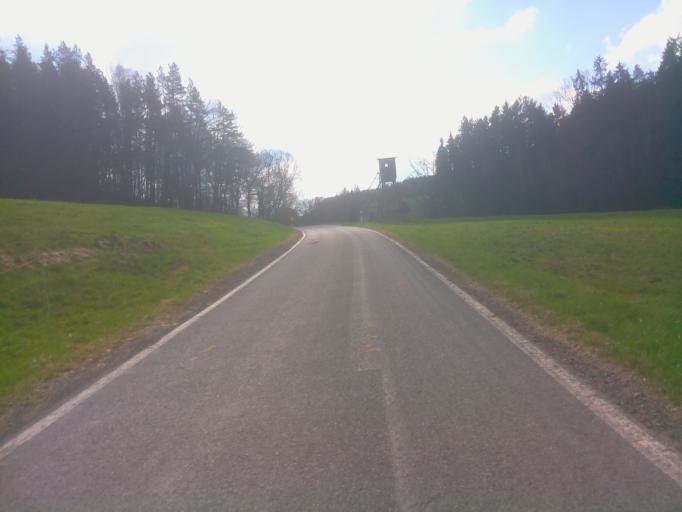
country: DE
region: Thuringia
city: Stanau
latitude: 50.7841
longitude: 11.7207
